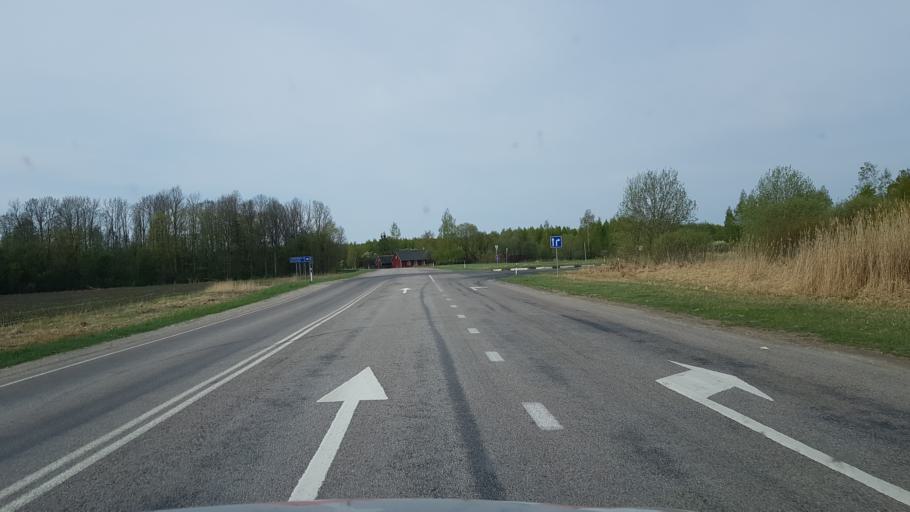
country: EE
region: Paernumaa
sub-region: Audru vald
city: Audru
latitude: 58.3933
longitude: 24.2804
